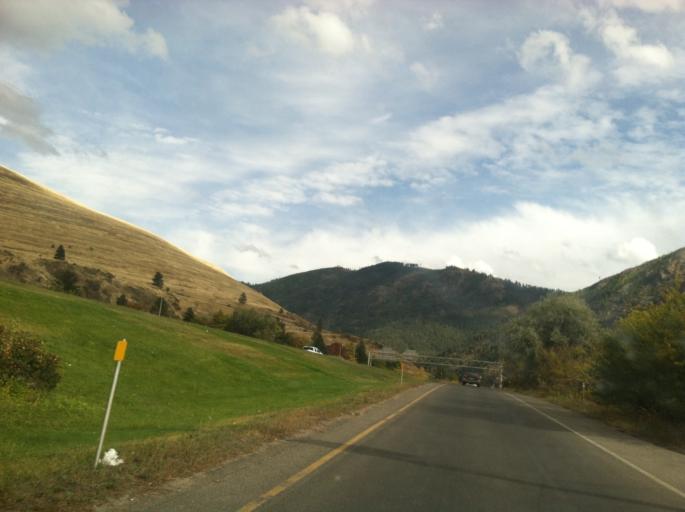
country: US
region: Montana
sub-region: Missoula County
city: Missoula
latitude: 46.8699
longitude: -113.9813
